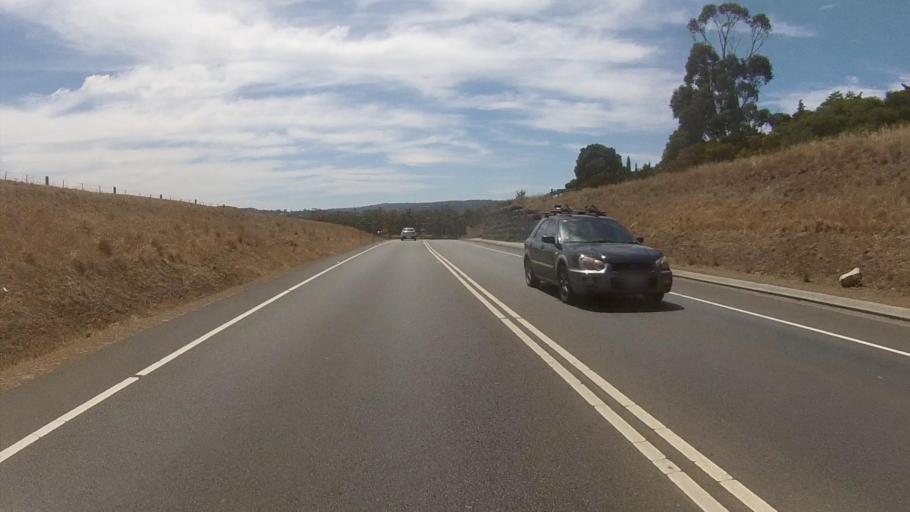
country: AU
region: Tasmania
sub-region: Kingborough
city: Kingston
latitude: -42.9895
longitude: 147.2859
